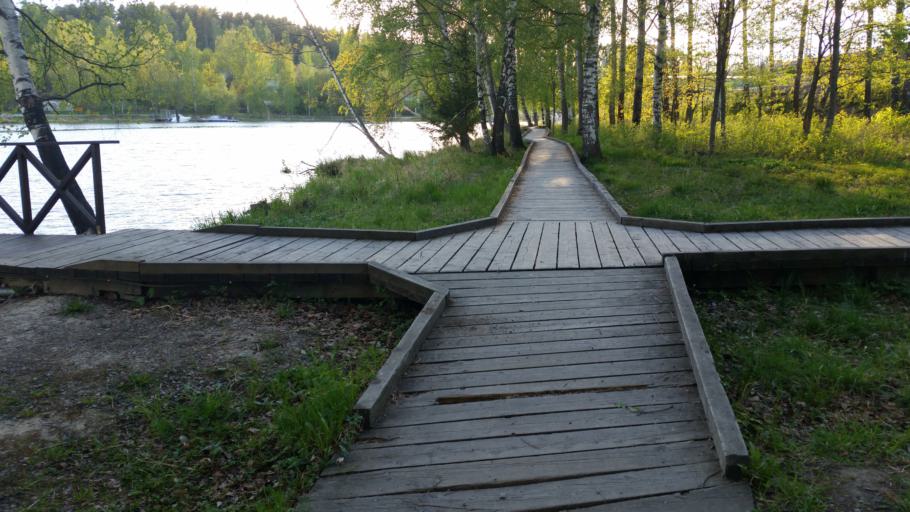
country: FI
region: Haeme
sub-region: Haemeenlinna
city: Haemeenlinna
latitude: 61.0141
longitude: 24.4504
